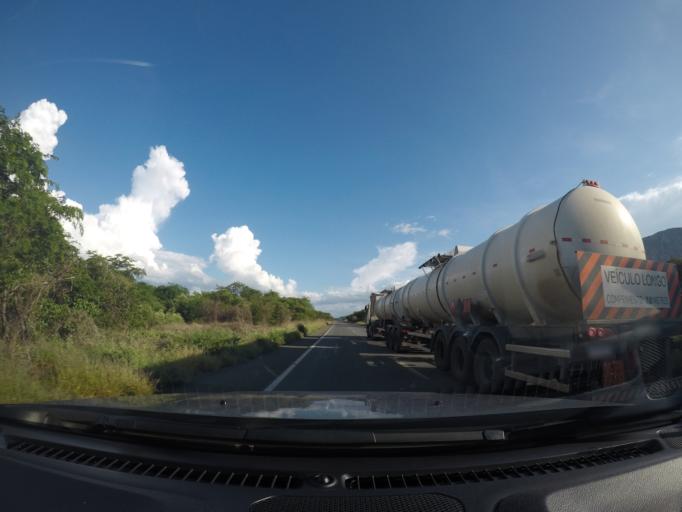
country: BR
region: Bahia
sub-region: Oliveira Dos Brejinhos
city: Oliveira dos Brejinhos
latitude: -12.0512
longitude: -42.9680
